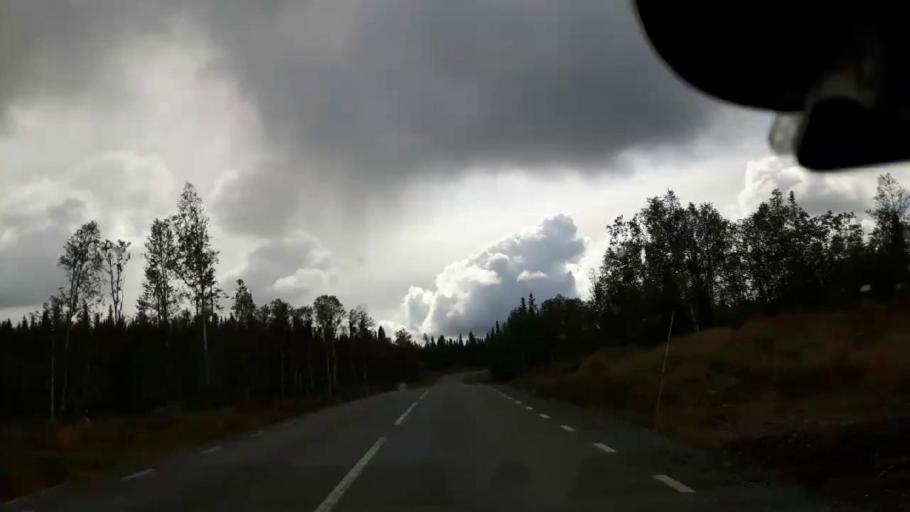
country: SE
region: Jaemtland
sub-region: Krokoms Kommun
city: Valla
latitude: 63.4383
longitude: 13.8224
